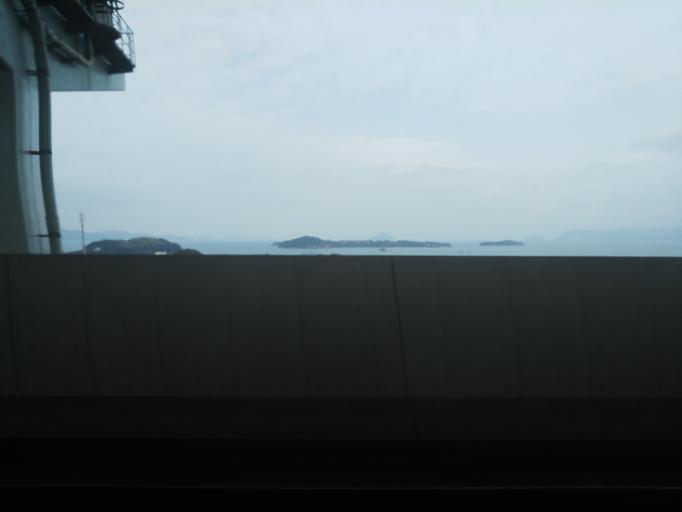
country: JP
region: Kagawa
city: Sakaidecho
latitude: 34.4206
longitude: 133.8038
